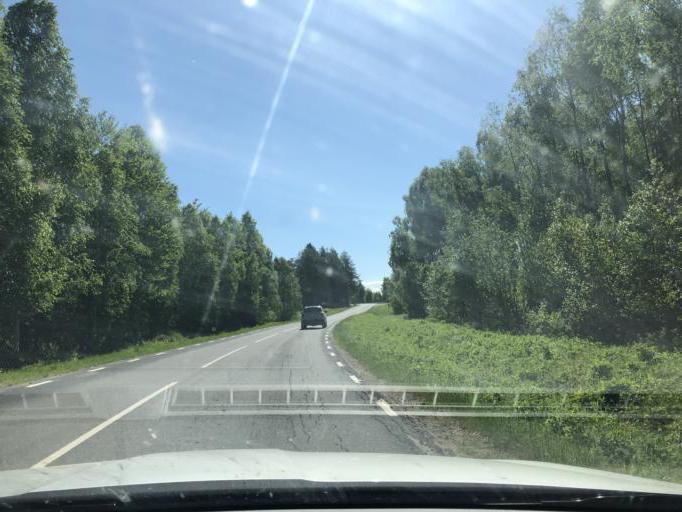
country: SE
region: Norrbotten
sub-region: Lulea Kommun
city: Gammelstad
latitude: 65.6592
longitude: 21.9925
